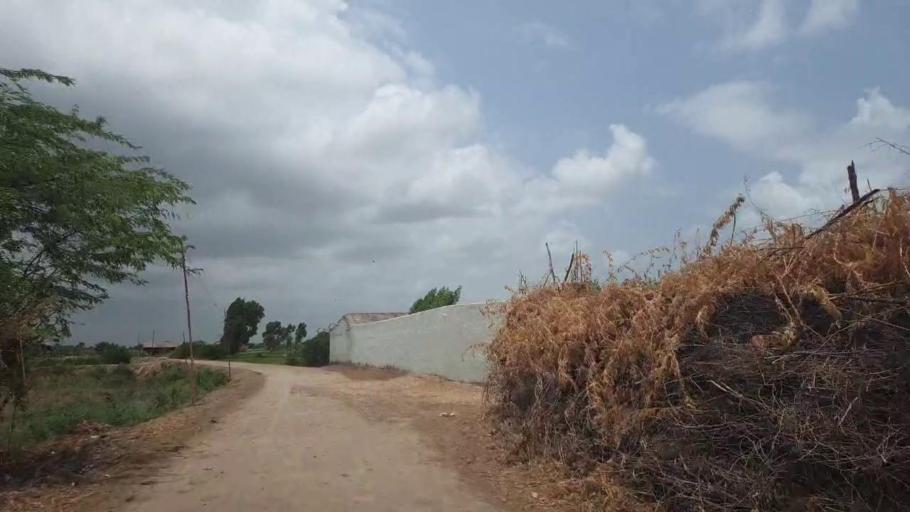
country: PK
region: Sindh
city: Badin
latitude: 24.6626
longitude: 68.9065
